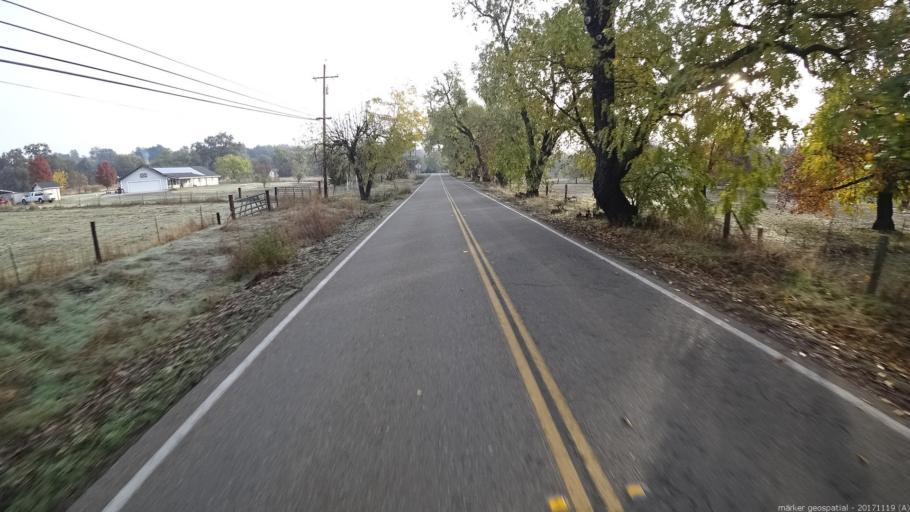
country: US
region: California
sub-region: Shasta County
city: Anderson
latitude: 40.4798
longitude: -122.3103
